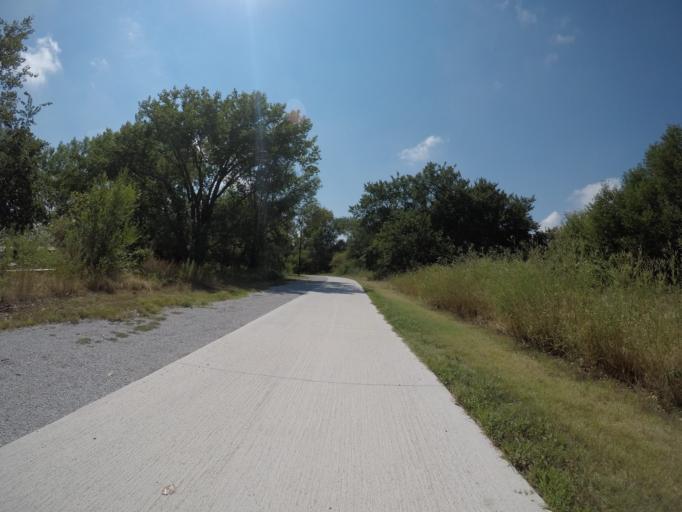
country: US
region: Nebraska
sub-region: Buffalo County
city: Kearney
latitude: 40.6726
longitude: -99.0344
